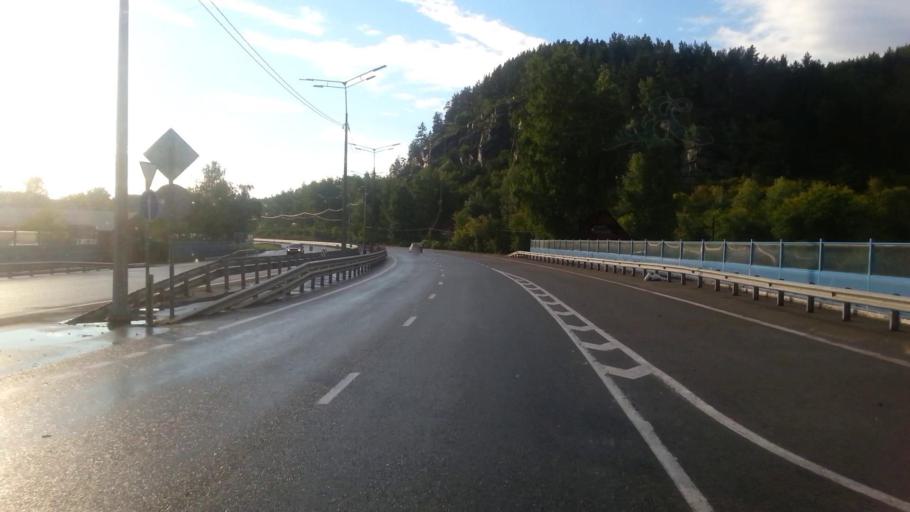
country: RU
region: Altay
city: Souzga
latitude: 51.9182
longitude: 85.8590
